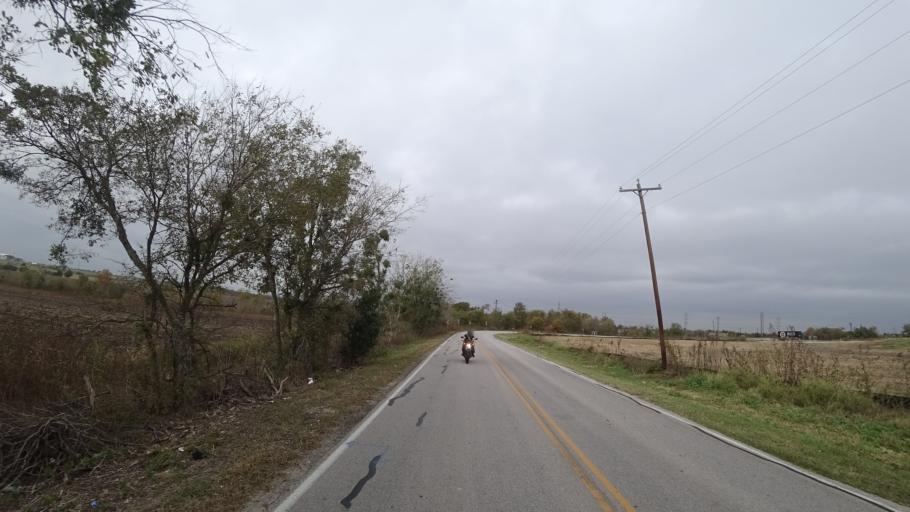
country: US
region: Texas
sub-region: Travis County
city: Manor
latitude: 30.4075
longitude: -97.5601
